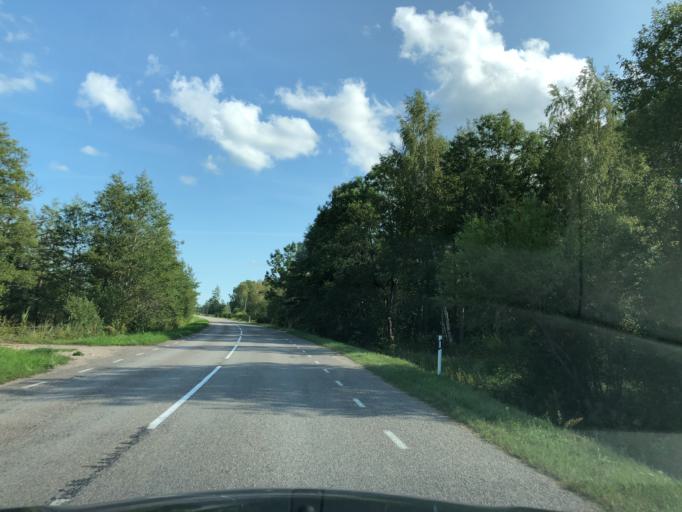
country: EE
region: Hiiumaa
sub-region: Kaerdla linn
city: Kardla
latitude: 58.7188
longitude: 22.5651
